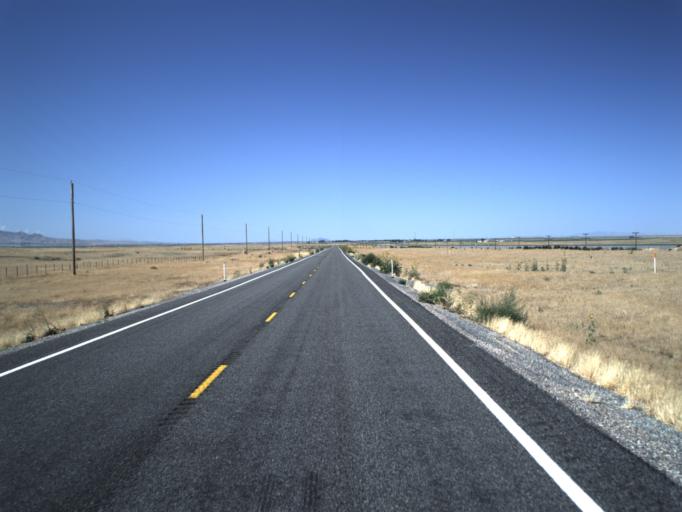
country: US
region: Utah
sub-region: Millard County
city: Delta
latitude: 39.6040
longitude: -112.3232
